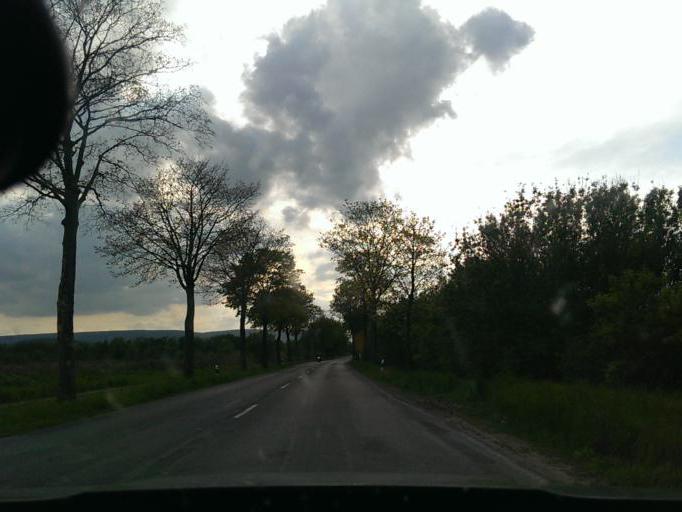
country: DE
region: Lower Saxony
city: Banteln
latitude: 52.0818
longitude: 9.7494
